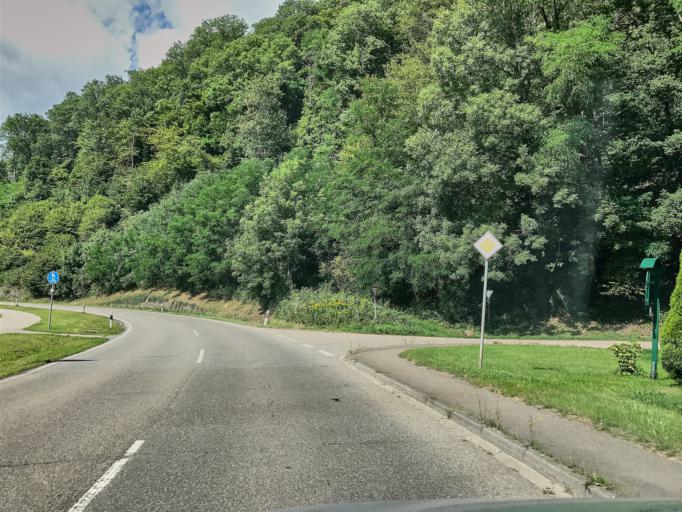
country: DE
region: Baden-Wuerttemberg
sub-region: Freiburg Region
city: Biberach
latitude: 48.3445
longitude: 8.0548
